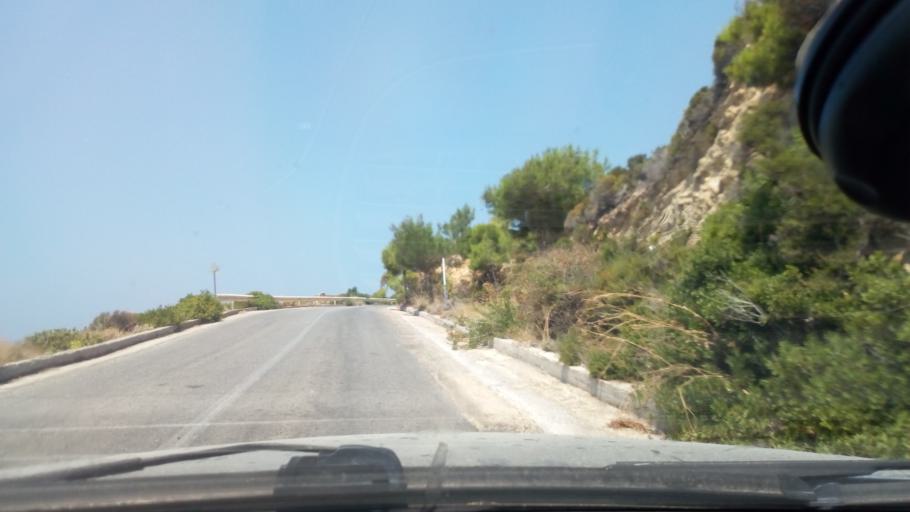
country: GR
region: North Aegean
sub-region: Nomos Samou
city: Agios Kirykos
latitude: 37.6335
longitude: 26.1222
